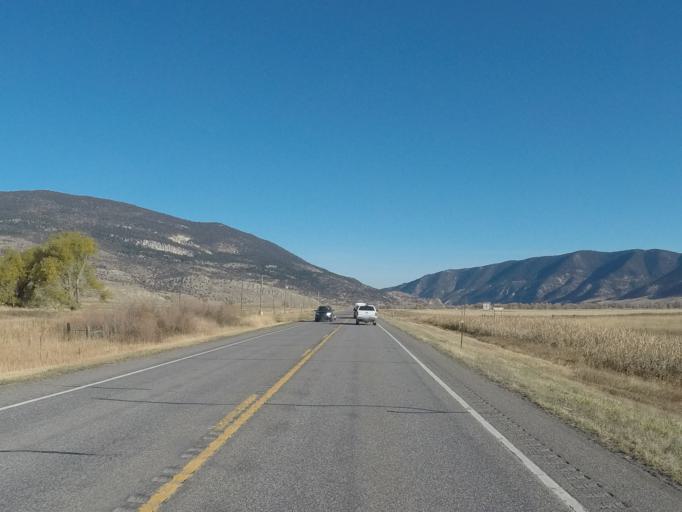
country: US
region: Montana
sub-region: Park County
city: Livingston
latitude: 45.5503
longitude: -110.5974
